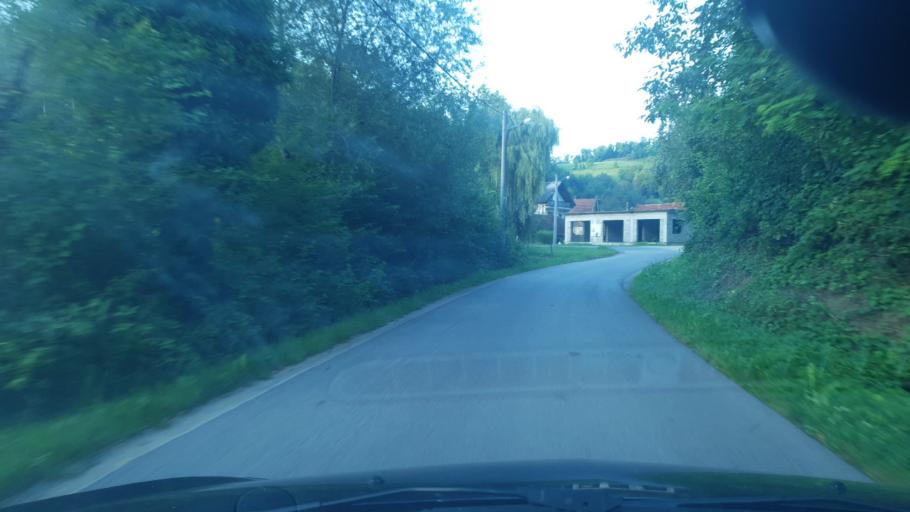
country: HR
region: Krapinsko-Zagorska
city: Zabok
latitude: 46.0498
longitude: 15.8881
